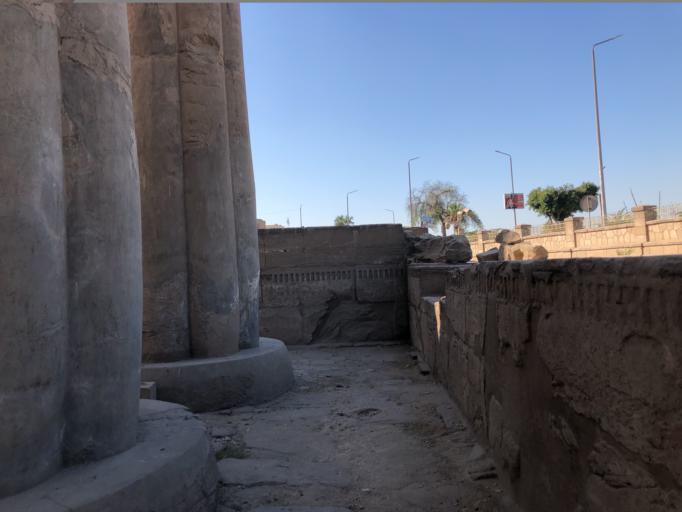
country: EG
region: Luxor
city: Luxor
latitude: 25.6992
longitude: 32.6385
